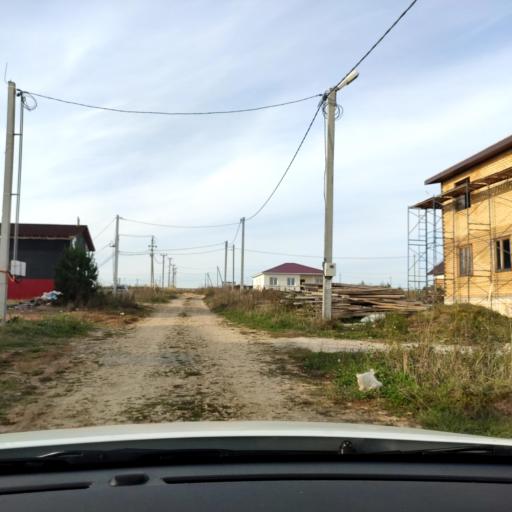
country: RU
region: Tatarstan
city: Vysokaya Gora
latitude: 55.9655
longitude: 49.2093
